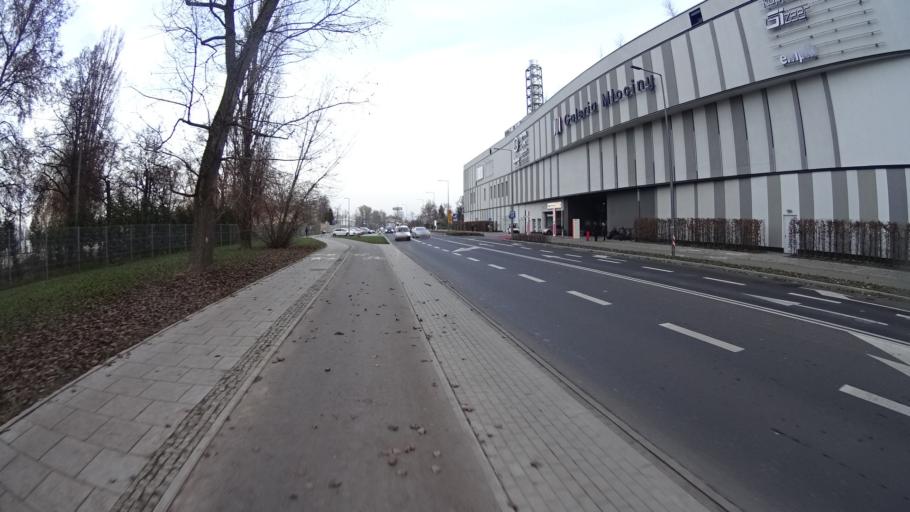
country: PL
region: Masovian Voivodeship
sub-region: Warszawa
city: Bielany
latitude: 52.2961
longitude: 20.9306
